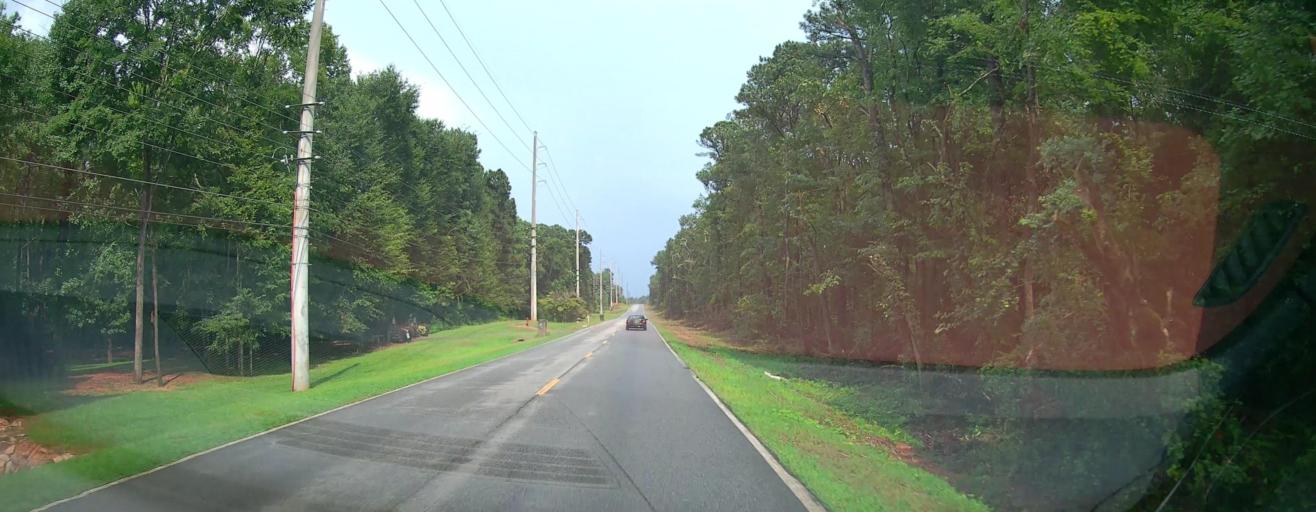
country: US
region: Georgia
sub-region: Houston County
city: Warner Robins
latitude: 32.6509
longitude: -83.6376
